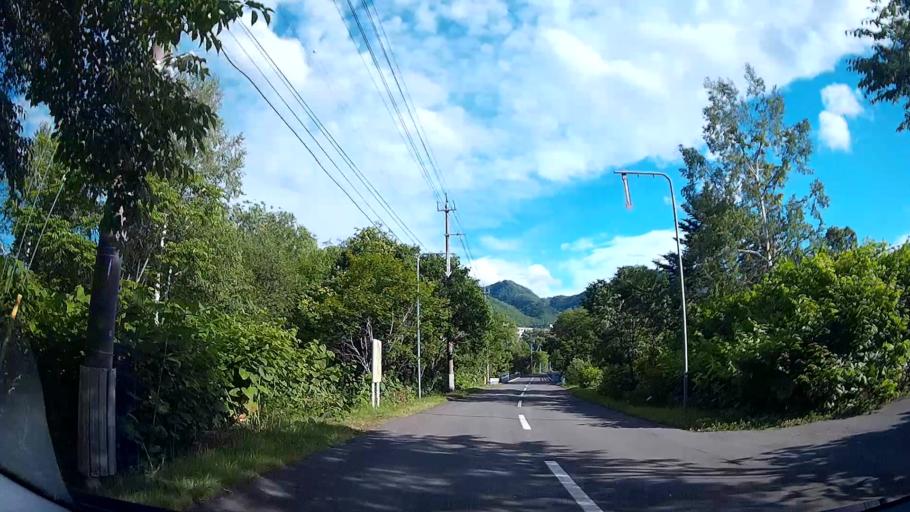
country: JP
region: Hokkaido
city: Sapporo
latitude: 42.9748
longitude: 141.1657
